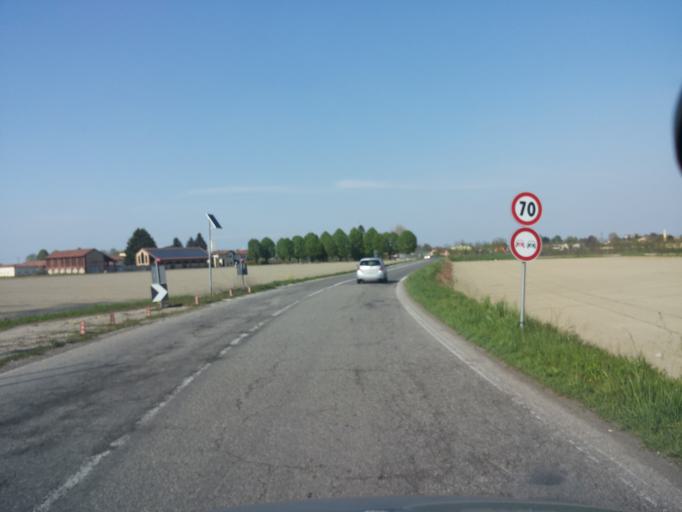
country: IT
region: Lombardy
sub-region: Provincia di Pavia
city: Castello d'Agogna
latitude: 45.2272
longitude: 8.6785
